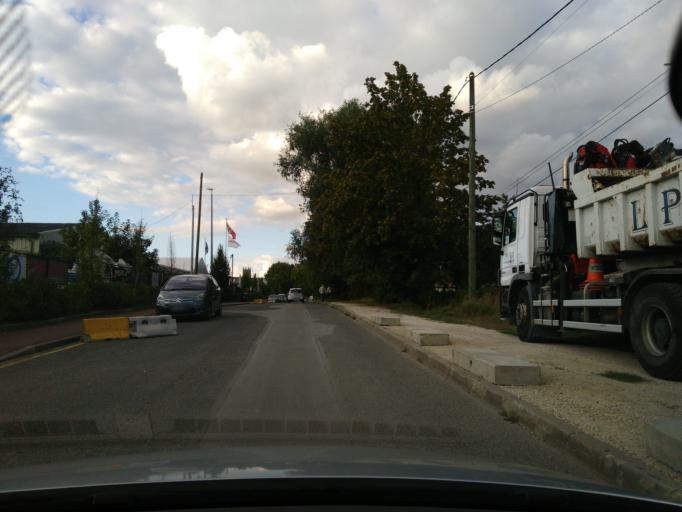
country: FR
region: Ile-de-France
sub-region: Departement de Seine-et-Marne
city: Meaux
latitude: 48.9505
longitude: 2.8839
